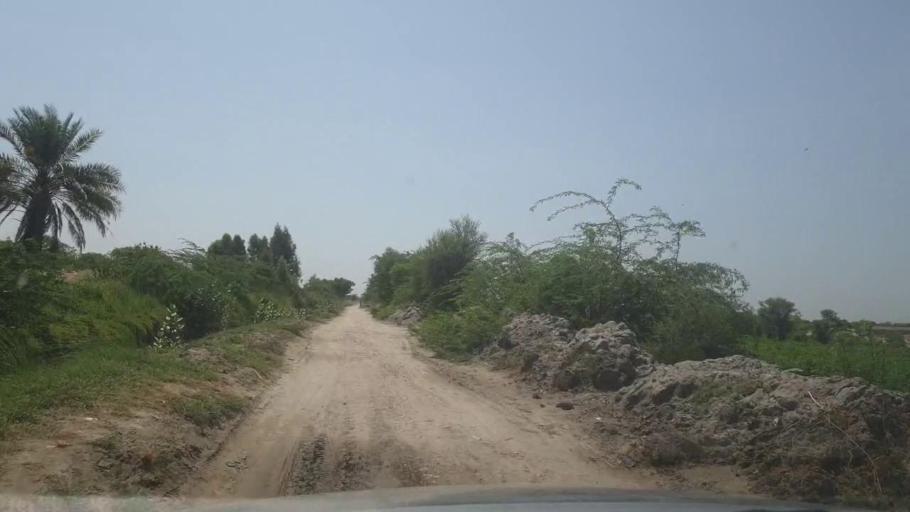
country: PK
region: Sindh
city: Khairpur
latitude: 27.3566
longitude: 69.0398
